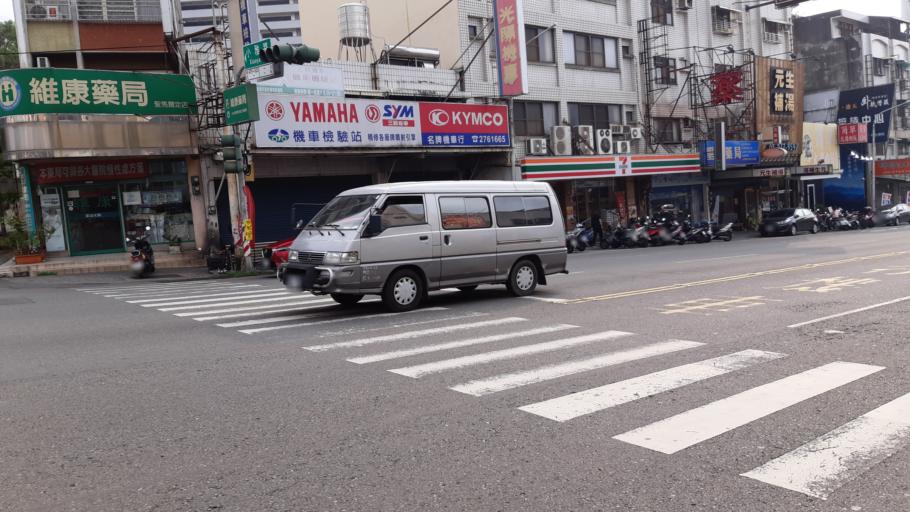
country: TW
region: Taiwan
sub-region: Chiayi
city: Jiayi Shi
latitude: 23.4775
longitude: 120.4680
